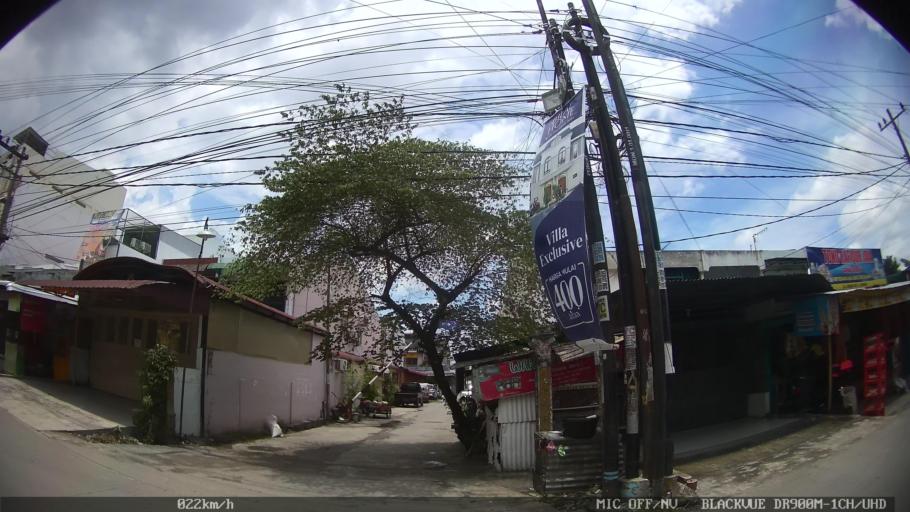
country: ID
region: North Sumatra
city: Medan
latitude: 3.6261
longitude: 98.6740
